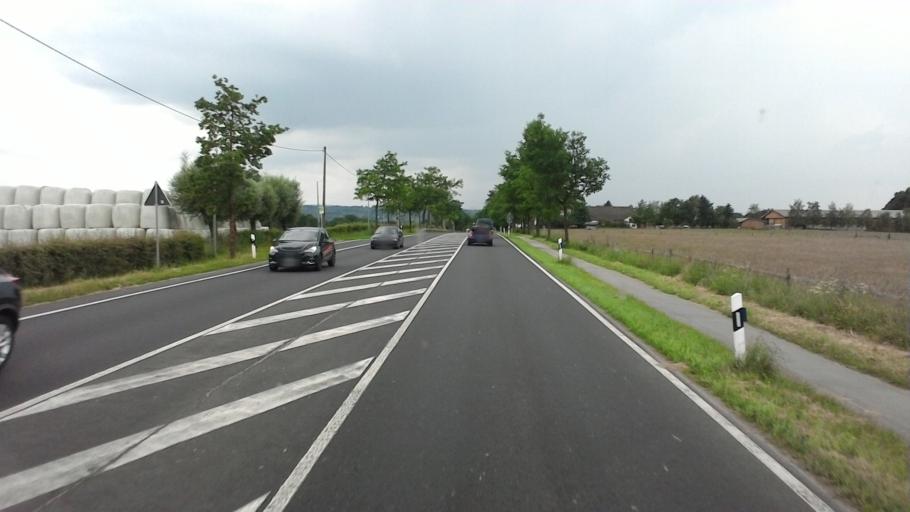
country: DE
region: North Rhine-Westphalia
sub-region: Regierungsbezirk Koln
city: Roetgen
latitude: 50.6602
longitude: 6.1895
